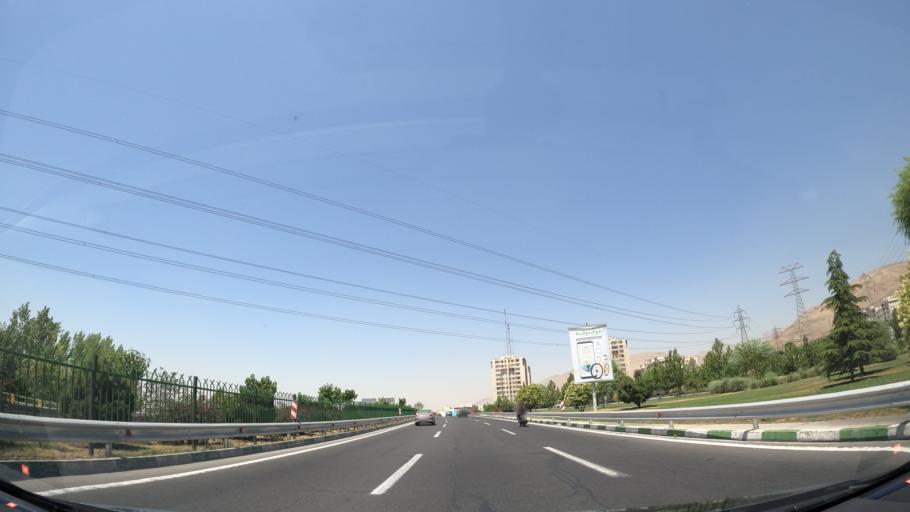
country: IR
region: Tehran
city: Tajrish
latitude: 35.7638
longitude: 51.2993
